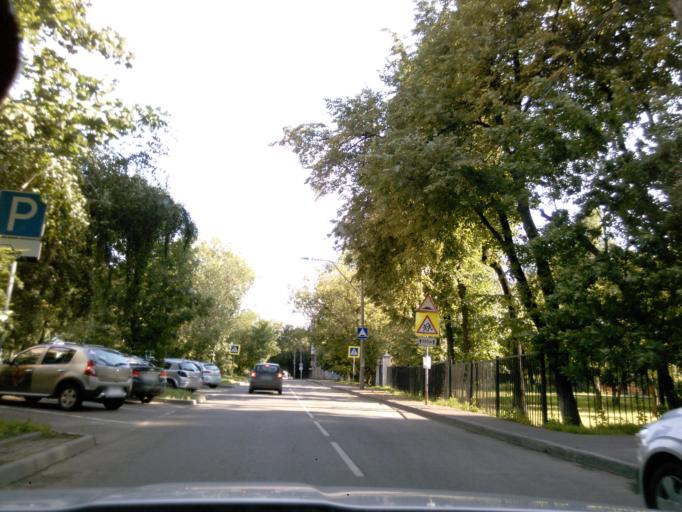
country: RU
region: Moskovskaya
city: Koptevo
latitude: 55.8285
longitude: 37.5255
